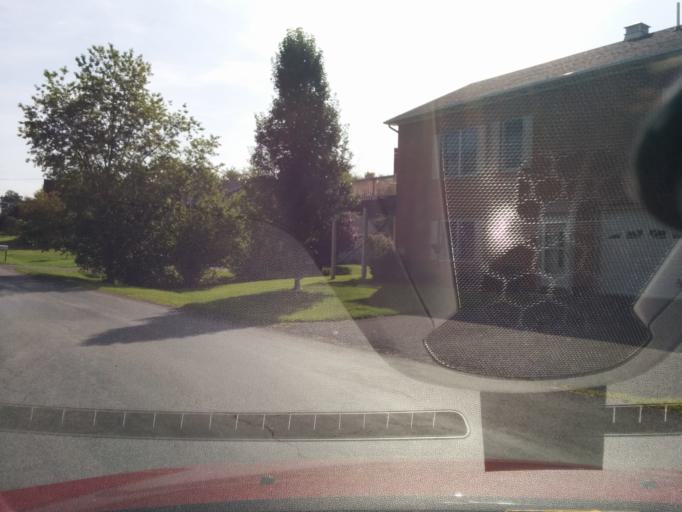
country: US
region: Virginia
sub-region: City of Lexington
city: Lexington
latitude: 37.7667
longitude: -79.4639
